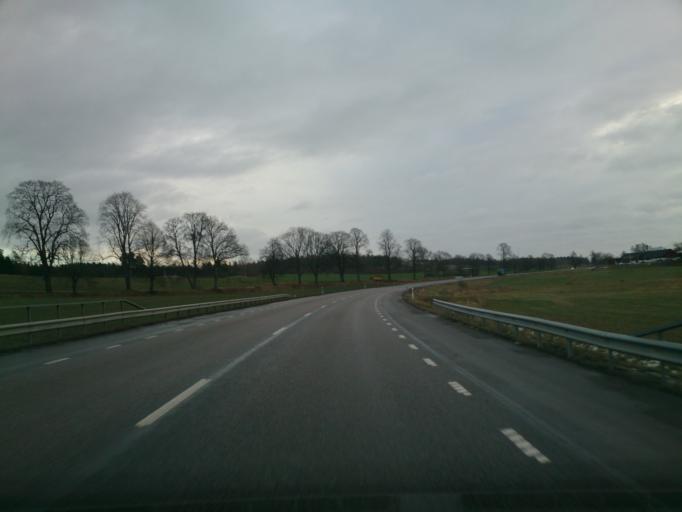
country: SE
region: OEstergoetland
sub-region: Atvidabergs Kommun
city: Atvidaberg
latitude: 58.2342
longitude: 15.9592
